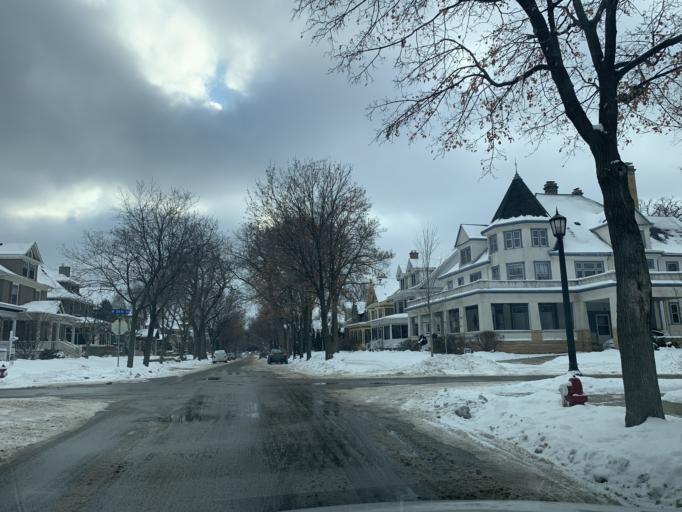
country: US
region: Minnesota
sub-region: Hennepin County
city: Minneapolis
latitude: 44.9593
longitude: -93.2982
